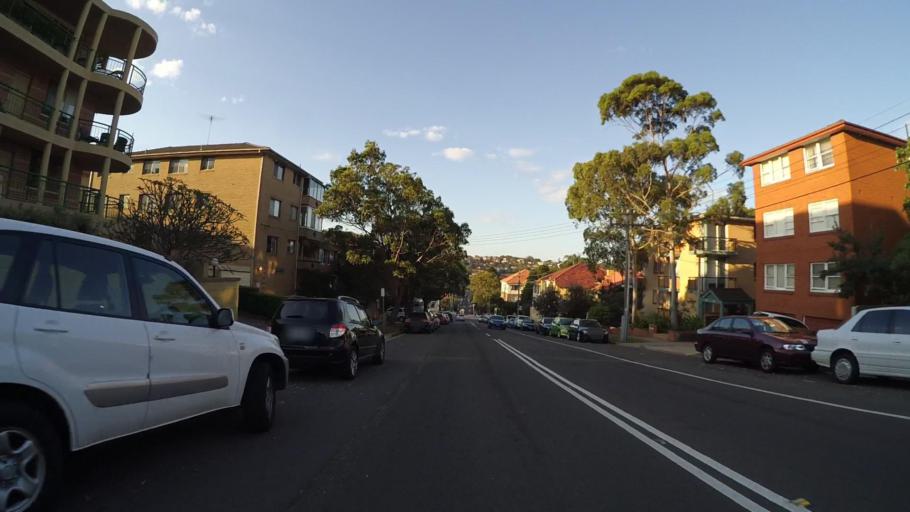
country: AU
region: New South Wales
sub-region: Randwick
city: Coogee
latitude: -33.9211
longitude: 151.2518
